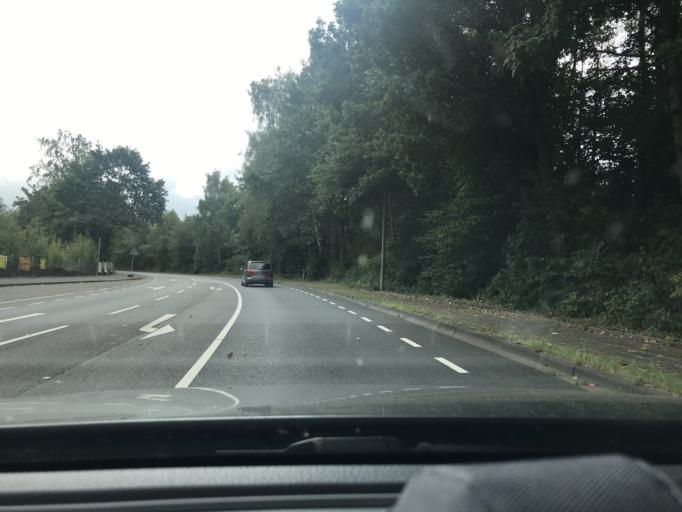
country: DE
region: North Rhine-Westphalia
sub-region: Regierungsbezirk Dusseldorf
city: Mettmann
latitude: 51.2445
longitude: 6.9776
